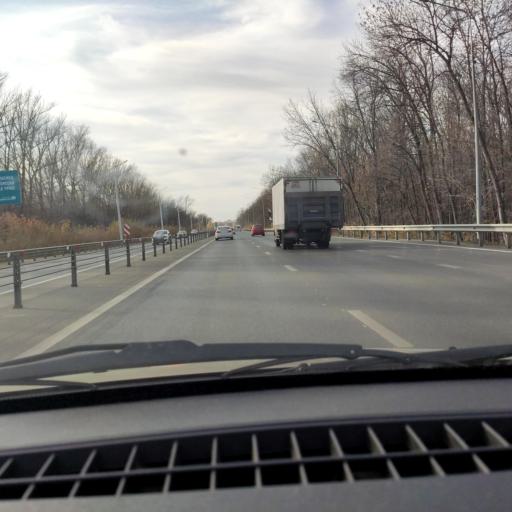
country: RU
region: Bashkortostan
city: Ufa
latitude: 54.7012
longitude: 55.9266
